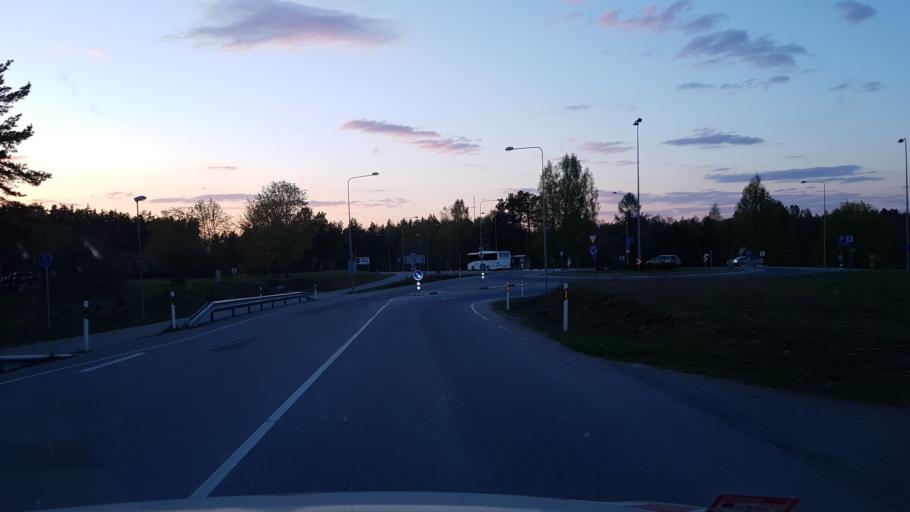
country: EE
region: Vorumaa
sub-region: Voru linn
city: Voru
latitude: 57.8152
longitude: 27.0293
